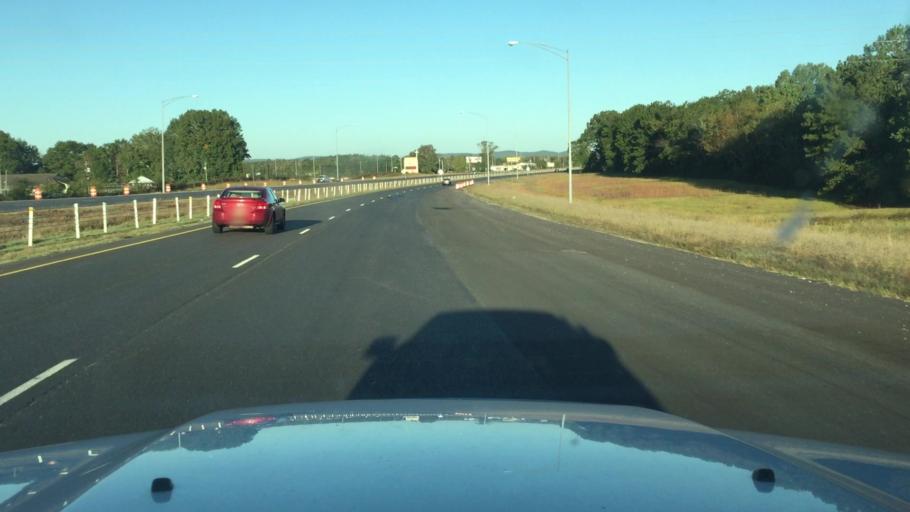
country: US
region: Alabama
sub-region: Etowah County
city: Rainbow City
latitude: 33.9924
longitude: -86.0429
